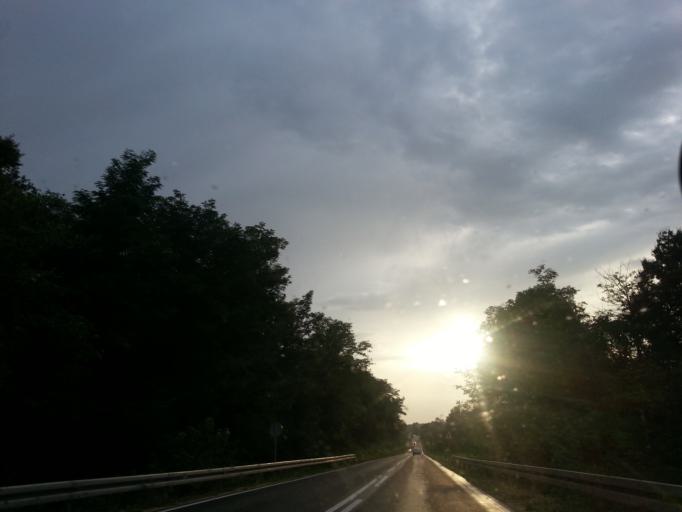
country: HR
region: Vukovarsko-Srijemska
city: Gunja
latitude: 44.8475
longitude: 18.9294
